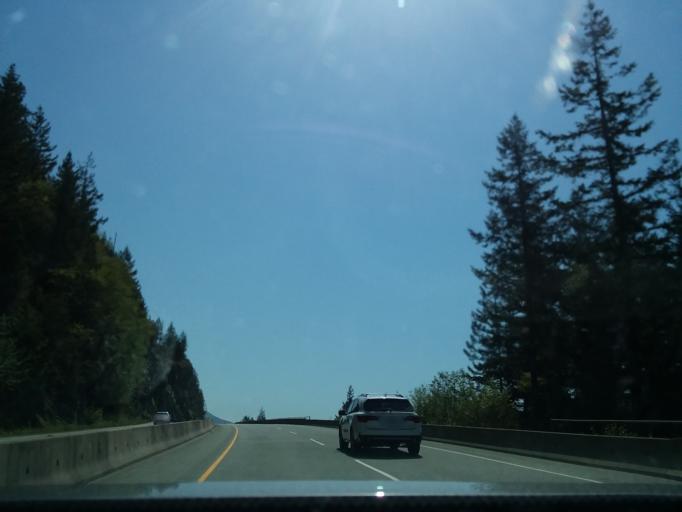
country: CA
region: British Columbia
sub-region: Greater Vancouver Regional District
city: Lions Bay
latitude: 49.5198
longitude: -123.2606
